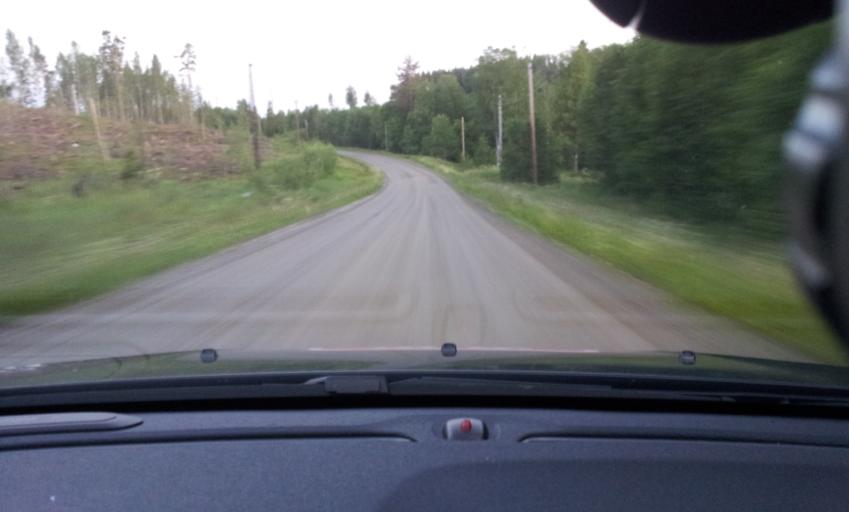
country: SE
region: Jaemtland
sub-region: Ragunda Kommun
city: Hammarstrand
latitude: 62.9091
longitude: 16.0943
